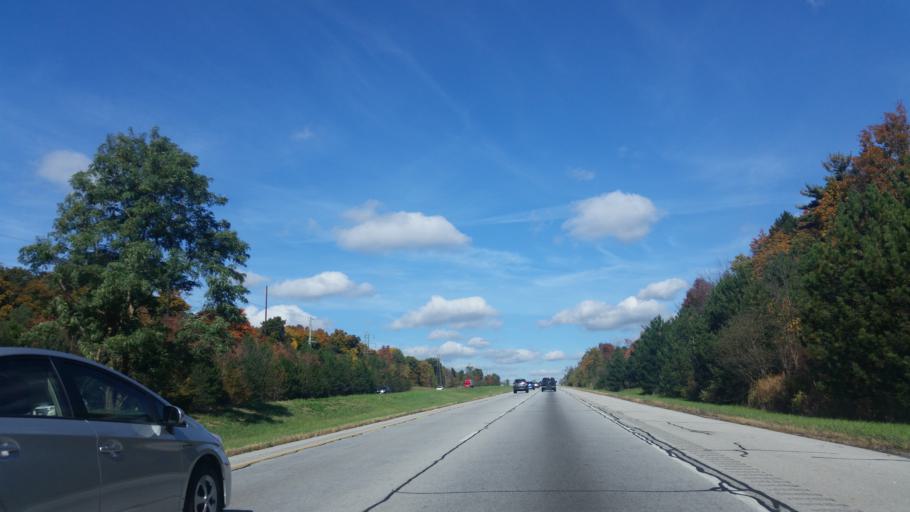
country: US
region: Ohio
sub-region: Summit County
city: Montrose-Ghent
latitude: 41.1761
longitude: -81.6257
